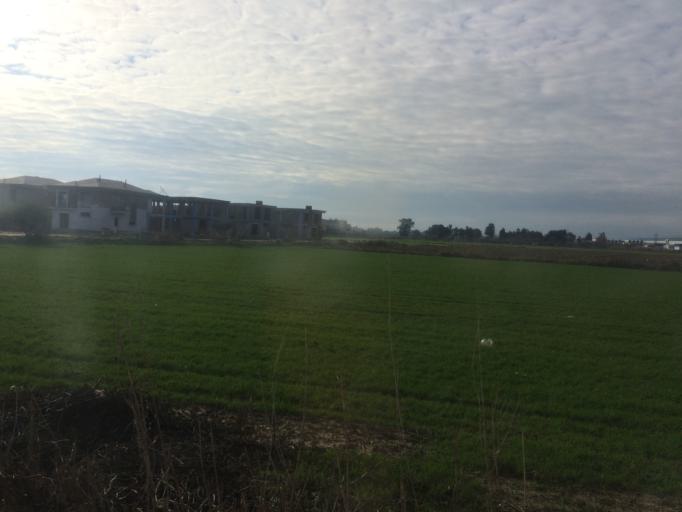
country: TR
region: Izmir
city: Menemen
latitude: 38.4989
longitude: 26.9599
